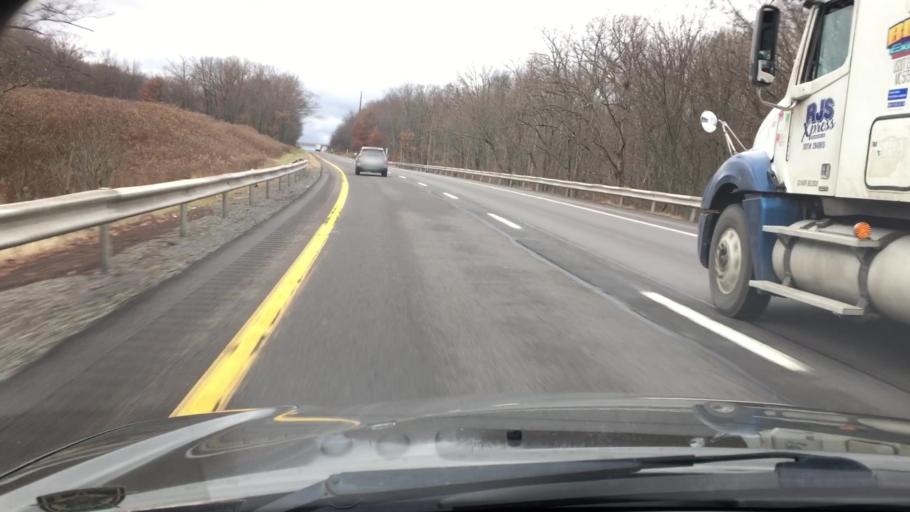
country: US
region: Pennsylvania
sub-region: Carbon County
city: Towamensing Trails
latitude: 41.0837
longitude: -75.6266
